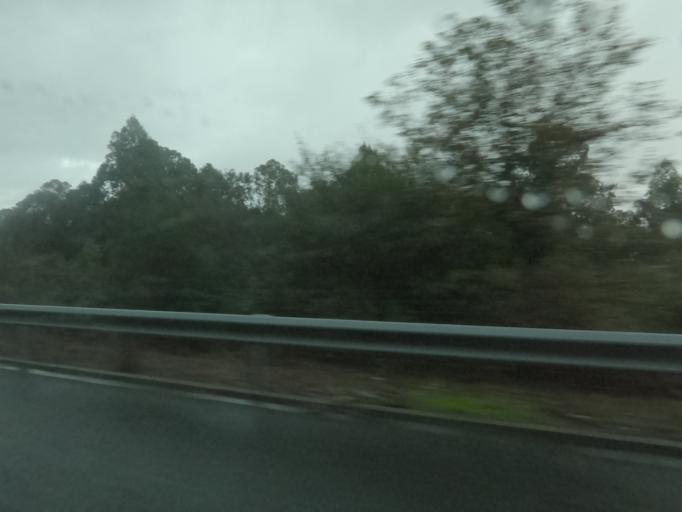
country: ES
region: Galicia
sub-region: Provincia de Pontevedra
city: Redondela
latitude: 42.3380
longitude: -8.6493
